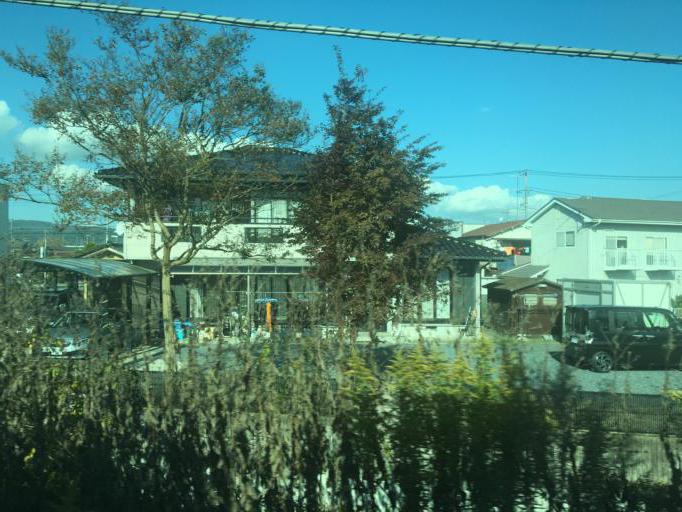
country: JP
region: Ibaraki
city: Kasama
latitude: 36.3726
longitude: 140.2482
